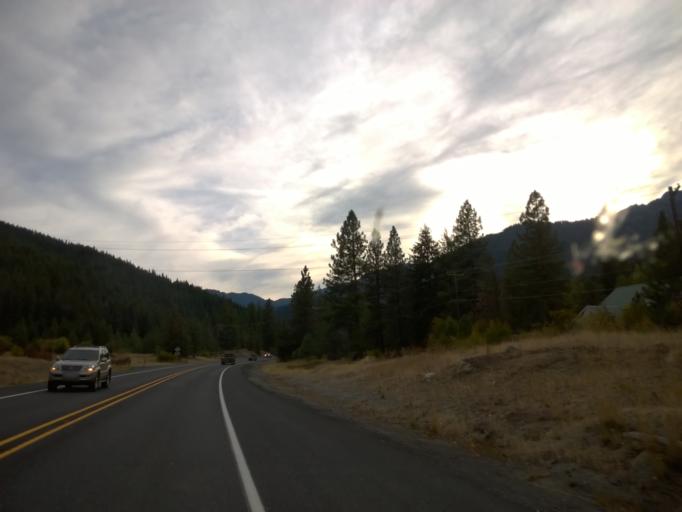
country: US
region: Washington
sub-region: Chelan County
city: Leavenworth
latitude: 47.4933
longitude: -120.6350
